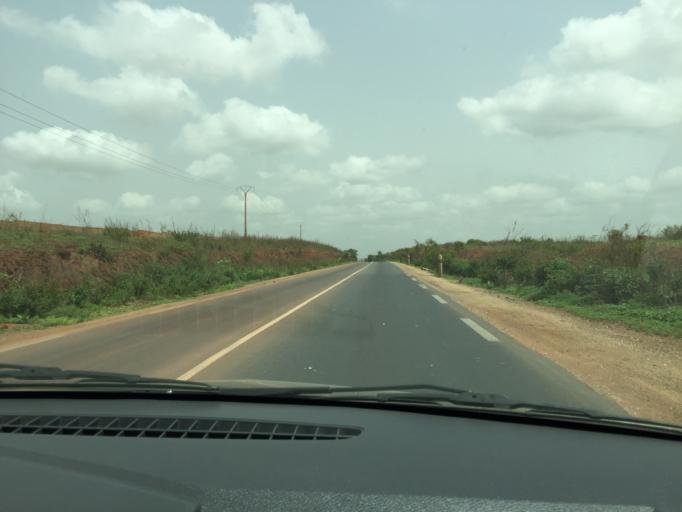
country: SN
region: Thies
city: Nguekhokh
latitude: 14.6151
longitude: -17.0526
